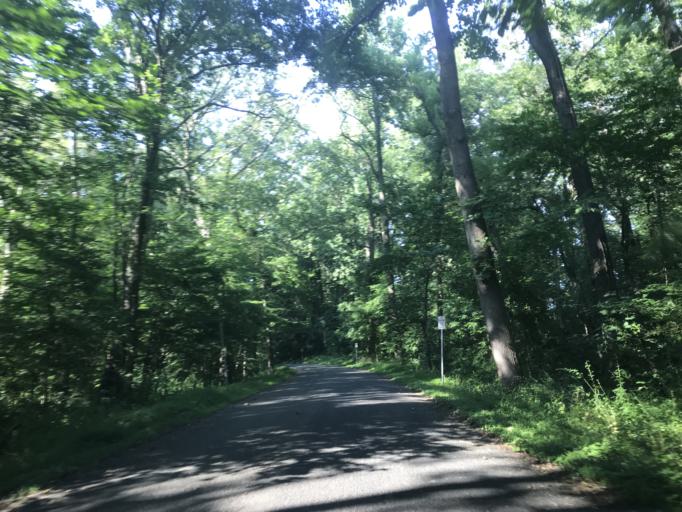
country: US
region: Maryland
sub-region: Harford County
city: Aberdeen
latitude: 39.5198
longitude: -76.1249
